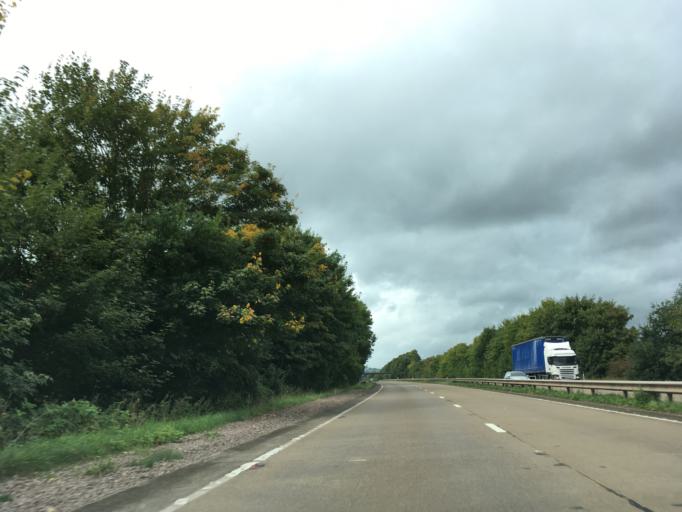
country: GB
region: Wales
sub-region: Monmouthshire
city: Llanarth
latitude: 51.7747
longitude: -2.8773
